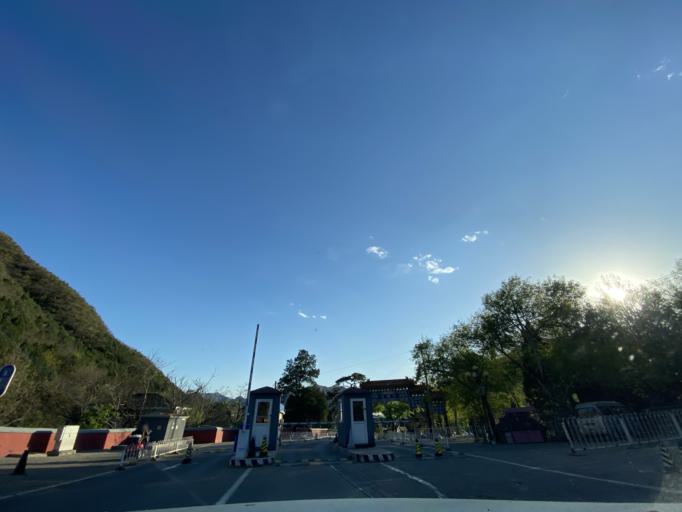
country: CN
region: Beijing
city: Tanzhesi
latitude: 39.8997
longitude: 116.0251
